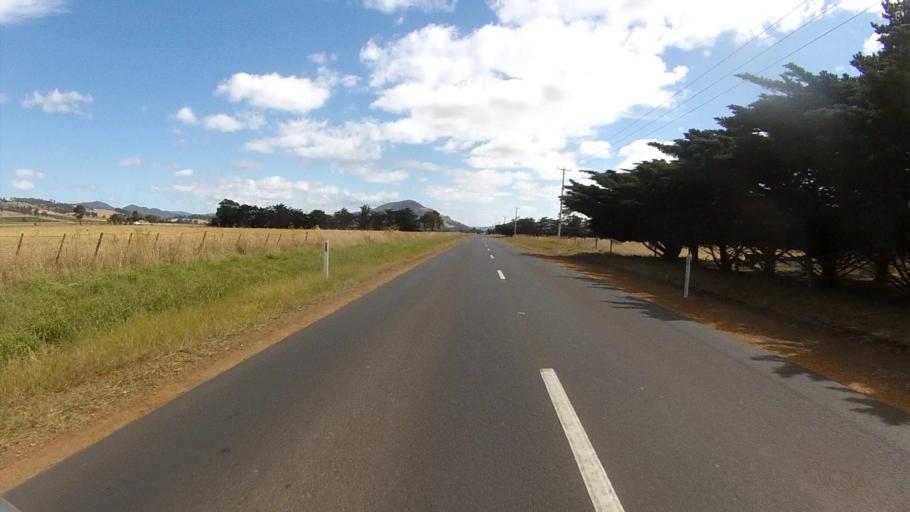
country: AU
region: Tasmania
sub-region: Clarence
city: Cambridge
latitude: -42.7076
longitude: 147.4297
